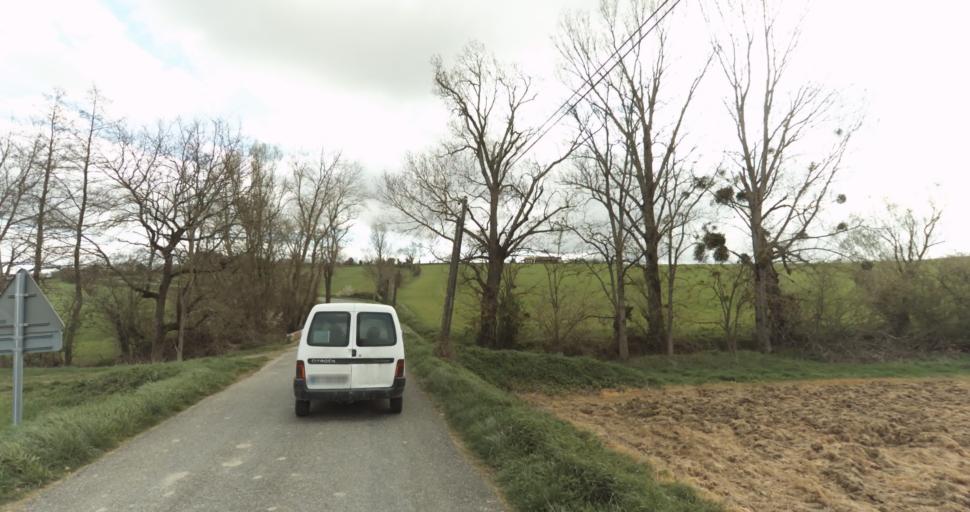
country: FR
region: Midi-Pyrenees
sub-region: Departement de la Haute-Garonne
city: Auterive
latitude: 43.3772
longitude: 1.4845
